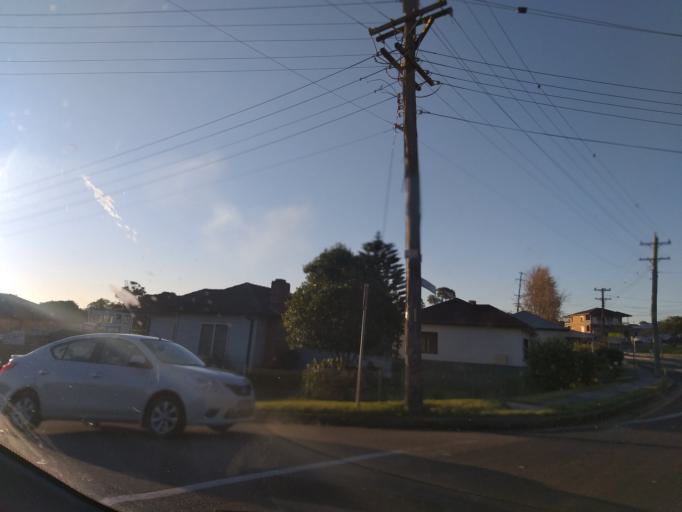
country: AU
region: New South Wales
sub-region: Wollongong
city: Port Kembla
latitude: -34.4909
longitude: 150.8941
